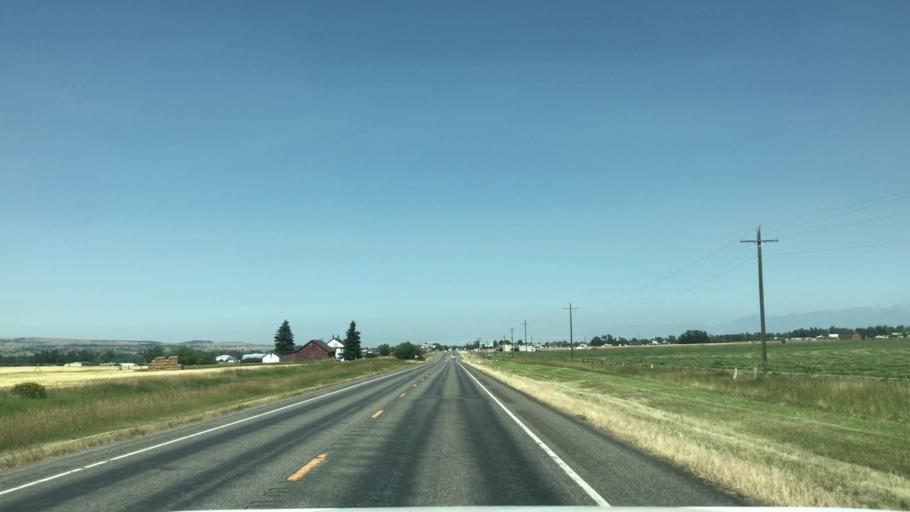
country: US
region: Montana
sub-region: Gallatin County
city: Four Corners
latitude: 45.5769
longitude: -111.1969
